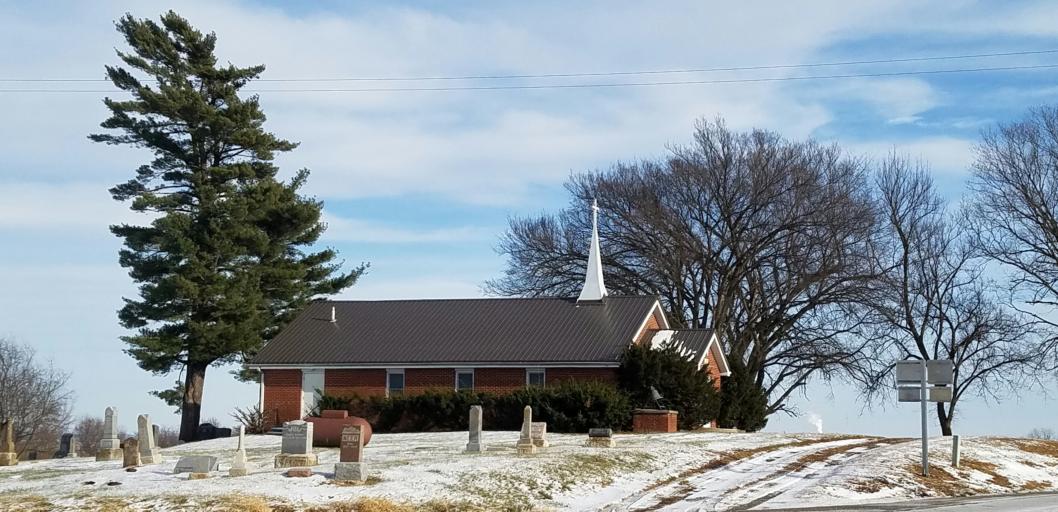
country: US
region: Missouri
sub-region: Carroll County
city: Carrollton
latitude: 39.2040
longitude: -93.4468
